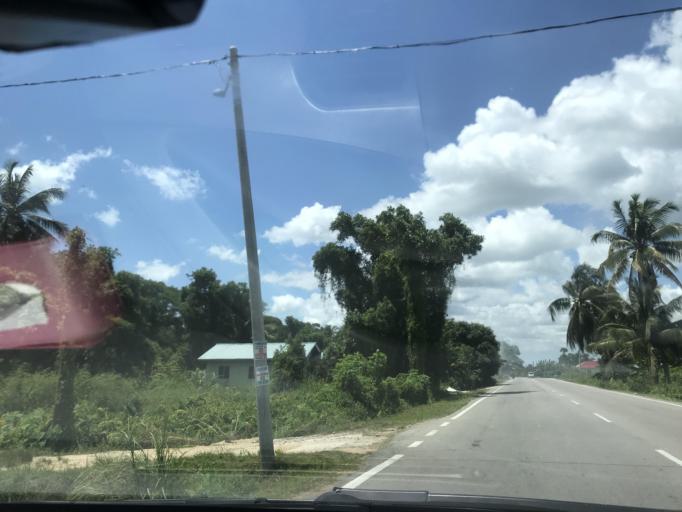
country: MY
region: Kelantan
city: Tumpat
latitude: 6.1960
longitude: 102.1360
